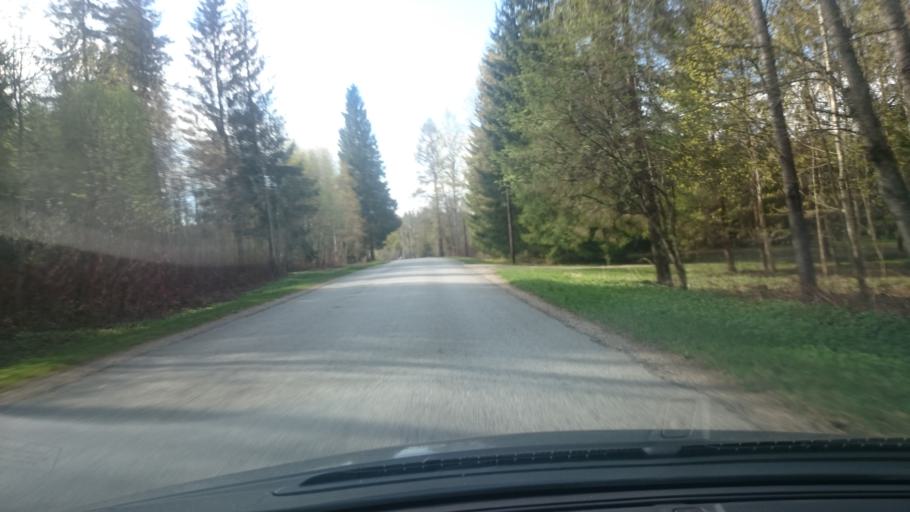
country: EE
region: Ida-Virumaa
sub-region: Toila vald
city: Voka
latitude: 59.1638
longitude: 27.5865
